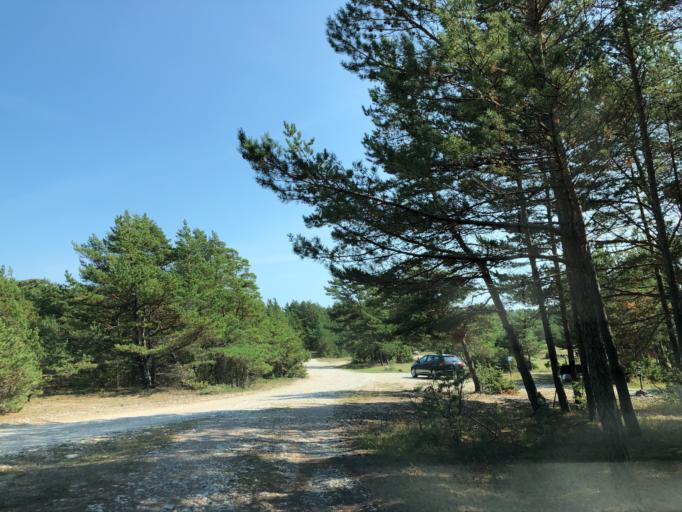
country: EE
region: Hiiumaa
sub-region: Kaerdla linn
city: Kardla
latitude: 58.9225
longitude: 22.0622
